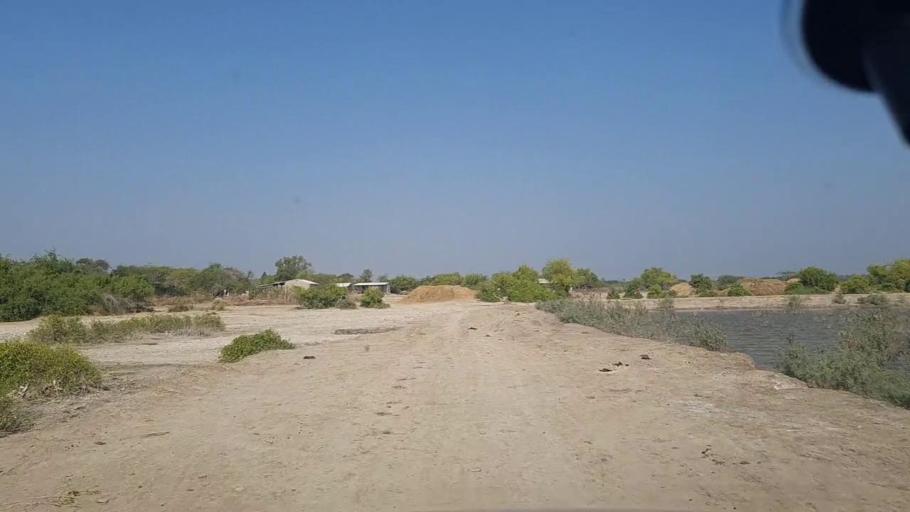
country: PK
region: Sindh
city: Chuhar Jamali
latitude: 24.5205
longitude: 67.8915
